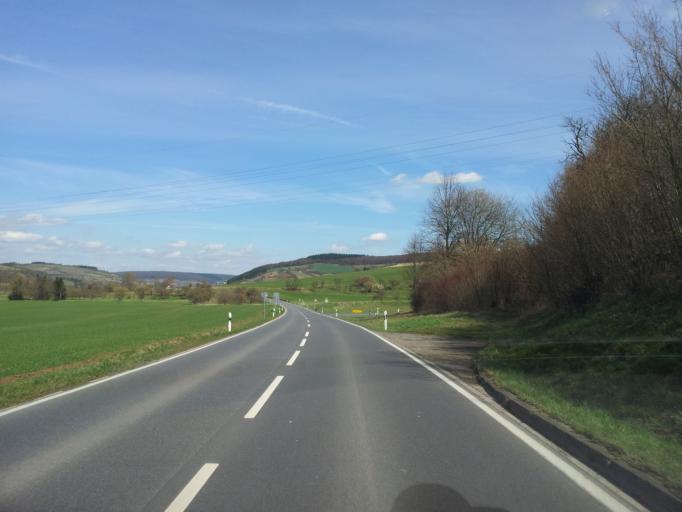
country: DE
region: Baden-Wuerttemberg
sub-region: Regierungsbezirk Stuttgart
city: Lauda-Konigshofen
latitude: 49.5133
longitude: 9.6972
